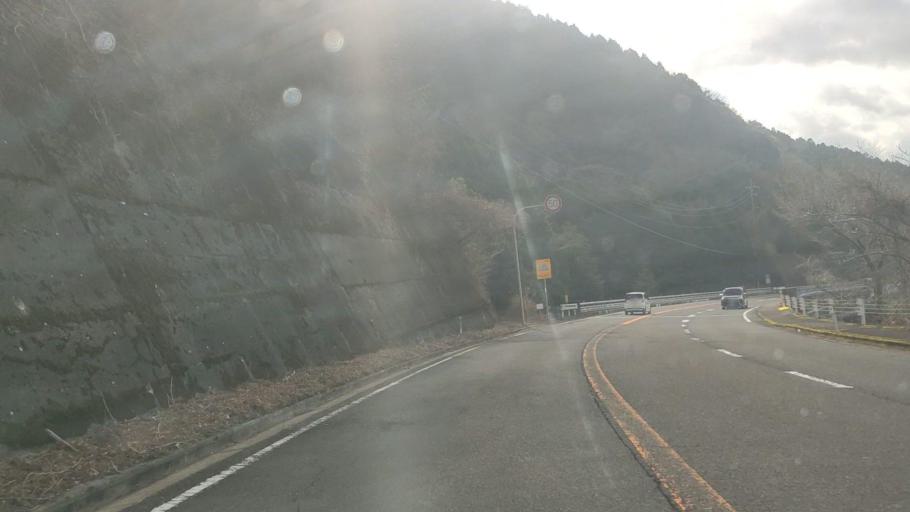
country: JP
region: Kumamoto
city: Hitoyoshi
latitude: 32.0778
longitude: 130.8032
